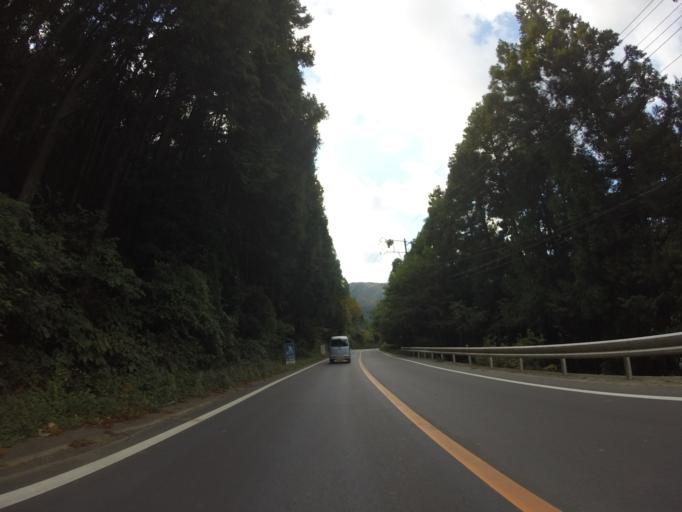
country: JP
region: Shizuoka
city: Kanaya
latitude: 34.8841
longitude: 138.1143
